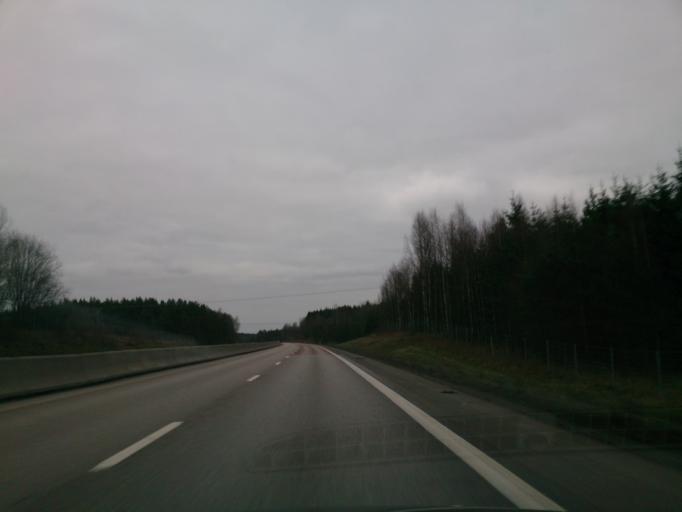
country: SE
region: OEstergoetland
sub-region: Norrkopings Kommun
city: Kimstad
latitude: 58.4989
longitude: 15.9807
